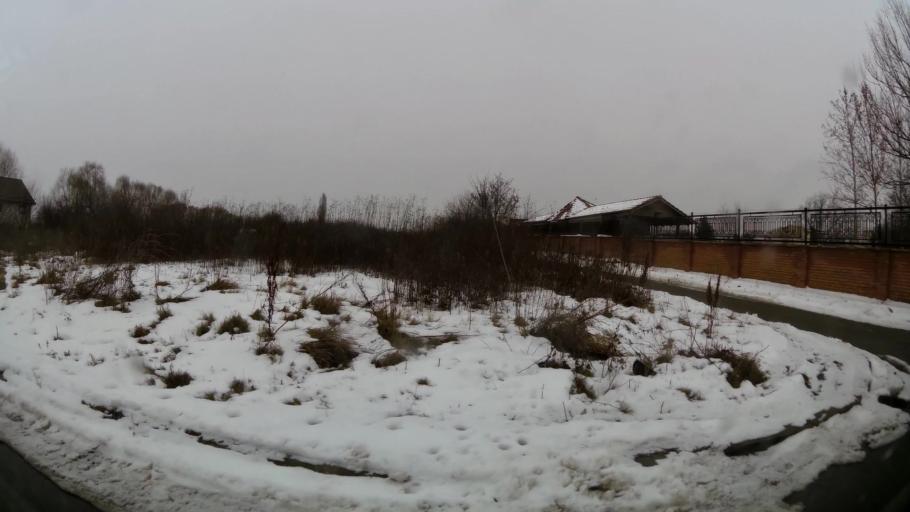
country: RO
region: Ilfov
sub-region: Comuna Mogosoaia
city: Mogosoaia
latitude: 44.5141
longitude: 26.0261
